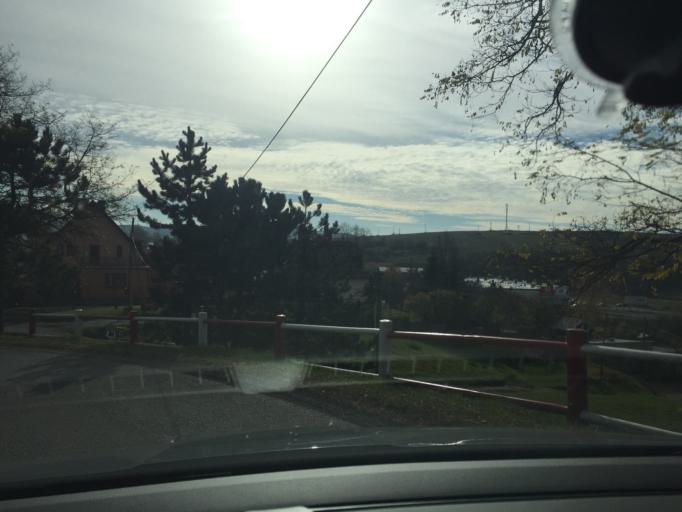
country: SK
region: Presovsky
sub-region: Okres Presov
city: Levoca
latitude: 49.0212
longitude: 20.5831
